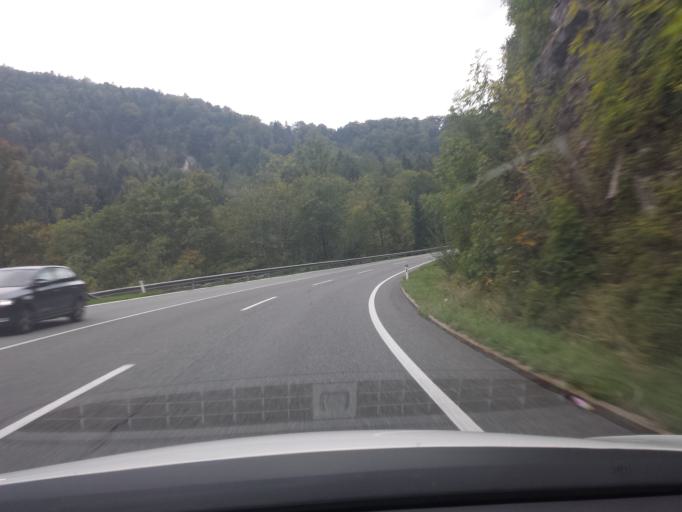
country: AT
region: Salzburg
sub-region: Politischer Bezirk Salzburg-Umgebung
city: Sankt Gilgen
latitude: 47.7725
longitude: 13.3519
